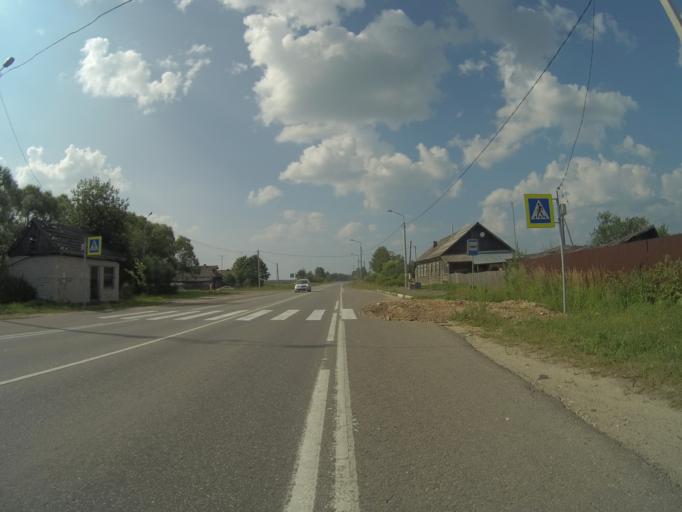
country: RU
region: Vladimir
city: Andreyevo
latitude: 55.8771
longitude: 41.1709
